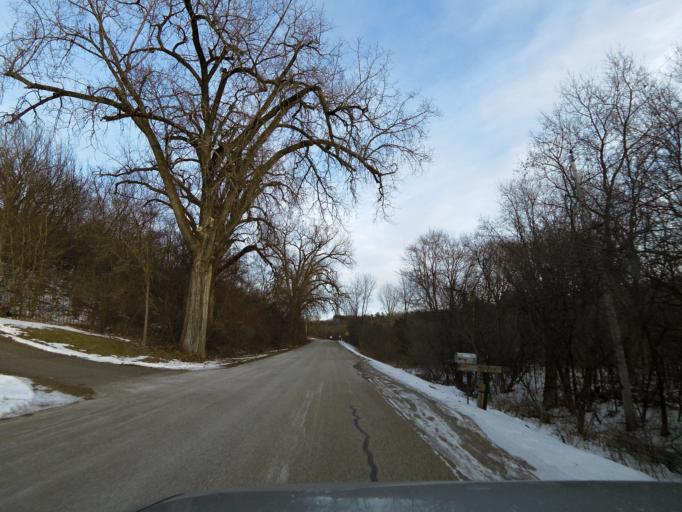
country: US
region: Minnesota
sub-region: Washington County
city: Afton
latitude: 44.9127
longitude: -92.8277
